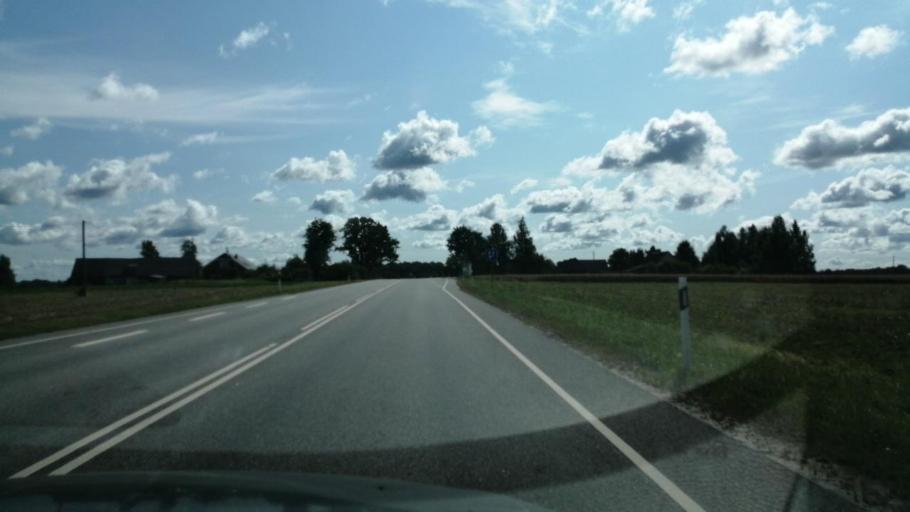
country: EE
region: Viljandimaa
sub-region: Viiratsi vald
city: Viiratsi
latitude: 58.3920
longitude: 25.7265
